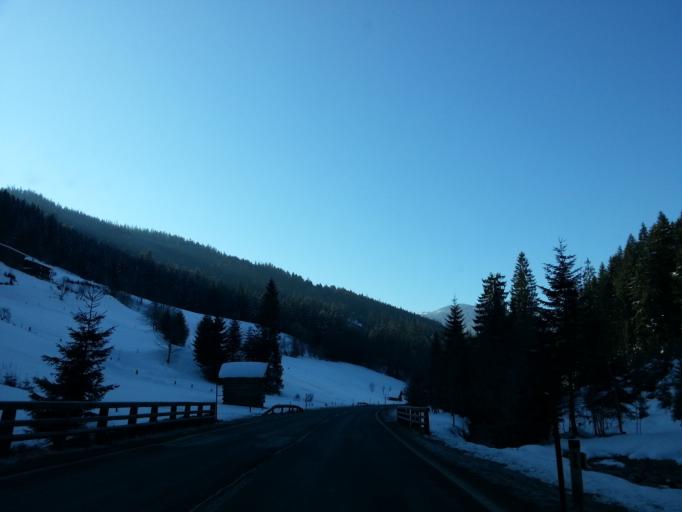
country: AT
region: Salzburg
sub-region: Politischer Bezirk Sankt Johann im Pongau
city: Eben im Pongau
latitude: 47.4426
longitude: 13.3627
